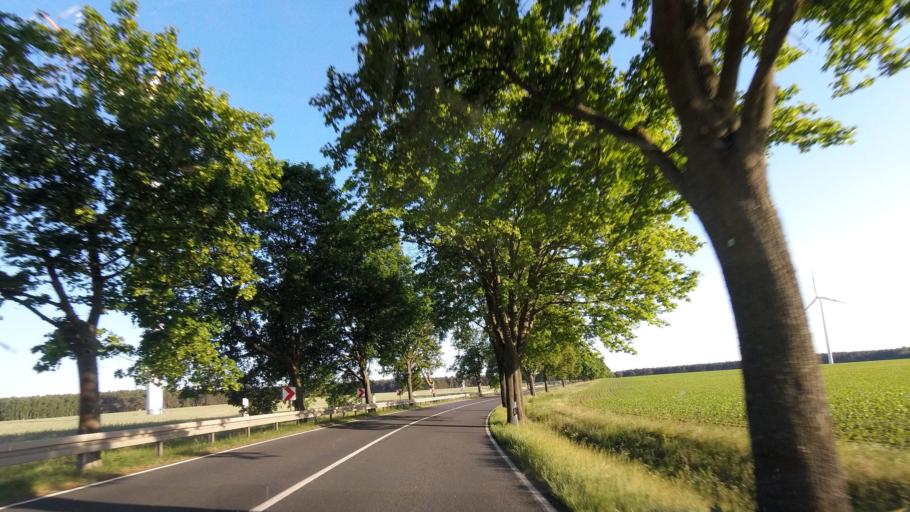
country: DE
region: Brandenburg
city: Golzow
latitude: 52.3117
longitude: 12.6093
